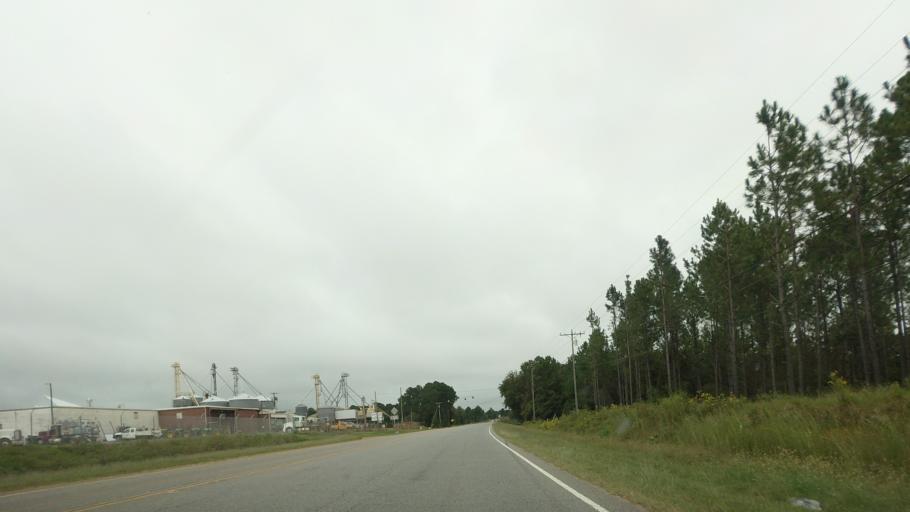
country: US
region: Georgia
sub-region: Irwin County
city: Ocilla
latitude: 31.6457
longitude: -83.2459
